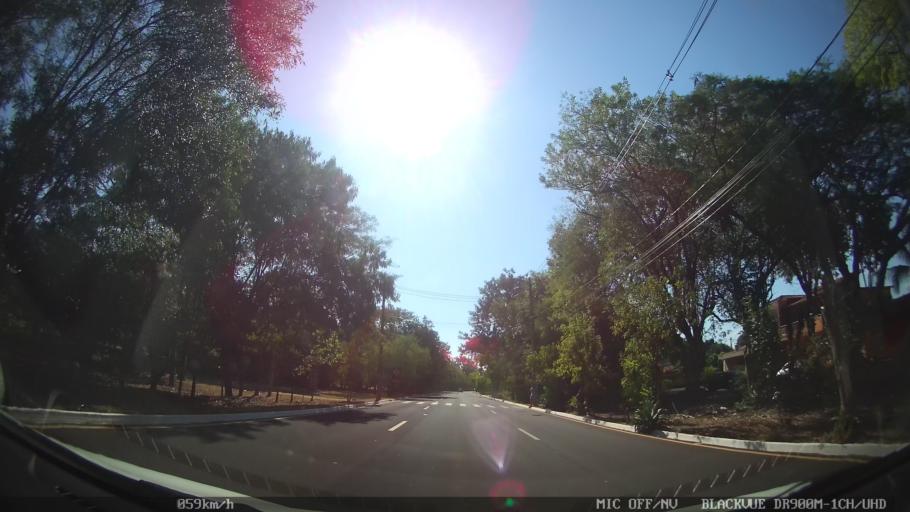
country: BR
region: Sao Paulo
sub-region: Ribeirao Preto
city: Ribeirao Preto
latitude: -21.2279
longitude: -47.7669
